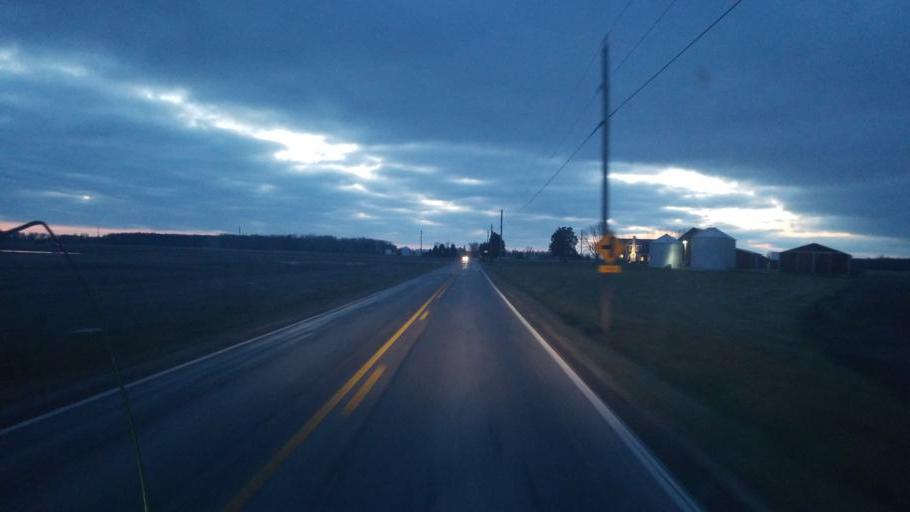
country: US
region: Ohio
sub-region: Marion County
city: Prospect
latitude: 40.4335
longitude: -83.0943
